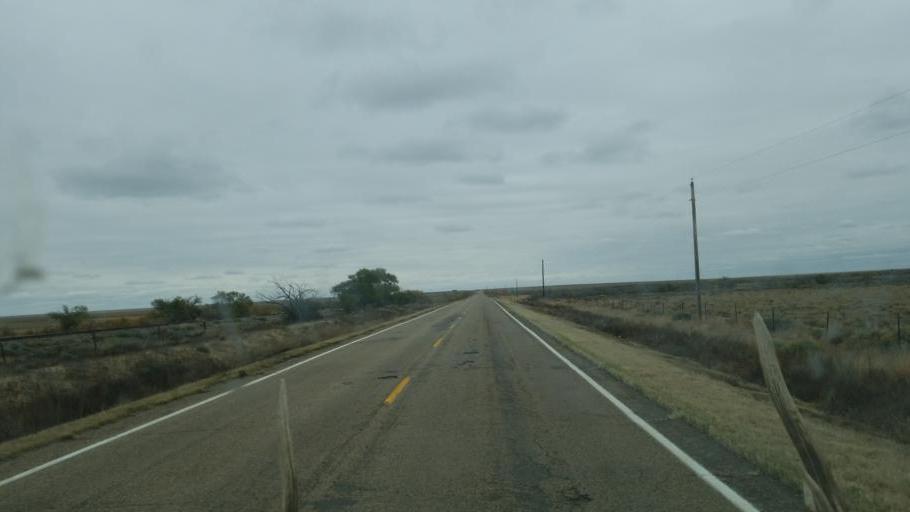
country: US
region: Colorado
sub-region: Crowley County
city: Ordway
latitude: 38.2375
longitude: -103.6442
